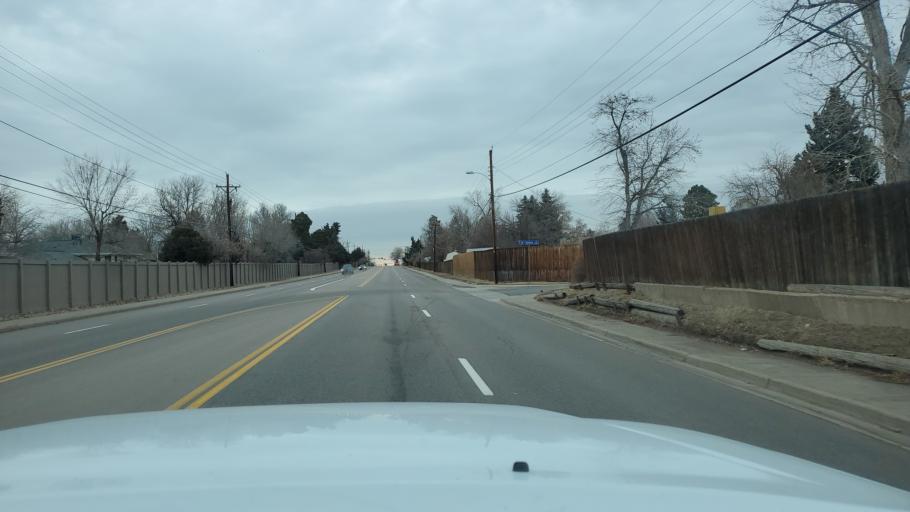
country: US
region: Colorado
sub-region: Arapahoe County
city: Southglenn
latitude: 39.5901
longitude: -104.9414
